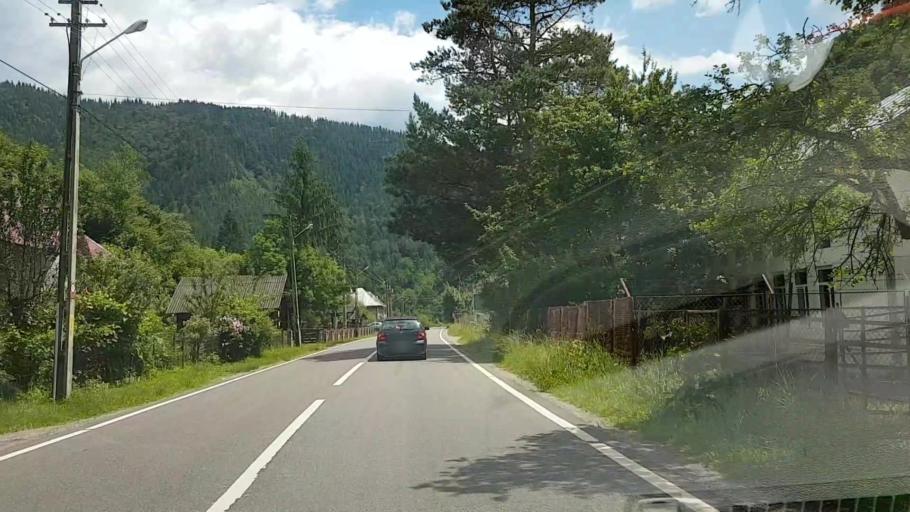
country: RO
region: Suceava
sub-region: Comuna Crucea
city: Crucea
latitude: 47.2833
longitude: 25.6381
